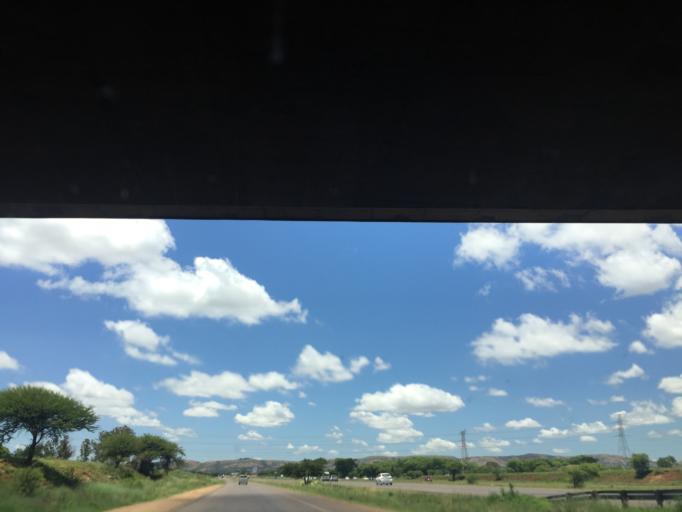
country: ZA
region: North-West
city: Ga-Rankuwa
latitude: -25.6293
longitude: 28.1115
